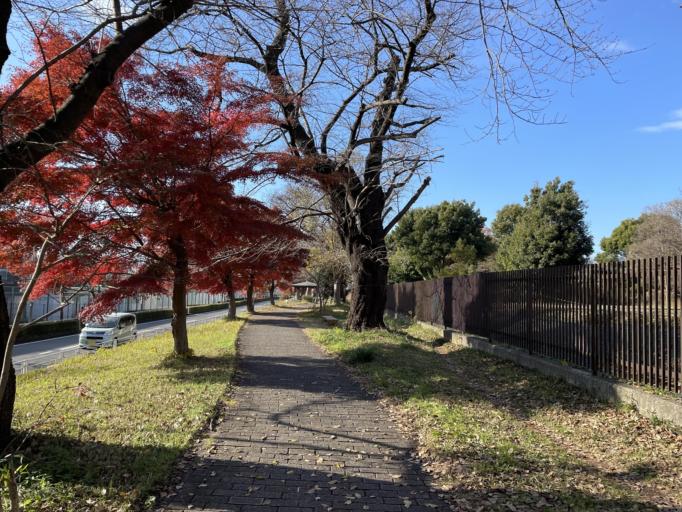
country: JP
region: Saitama
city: Asaka
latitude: 35.7777
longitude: 139.5928
